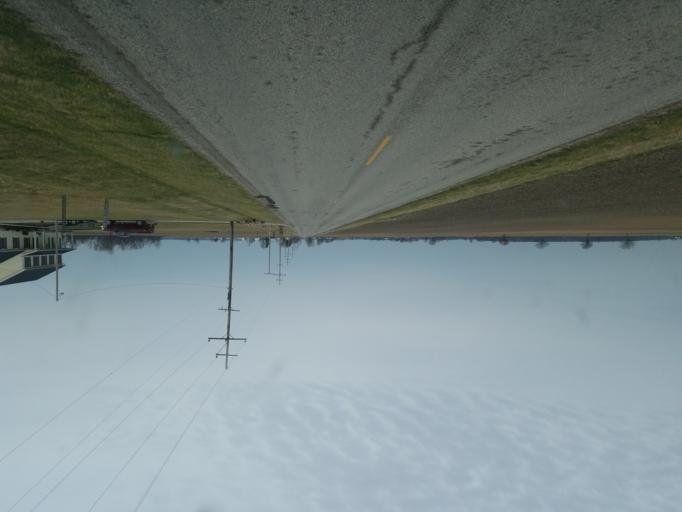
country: US
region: Ohio
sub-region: Marion County
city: Marion
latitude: 40.6550
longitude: -83.0732
